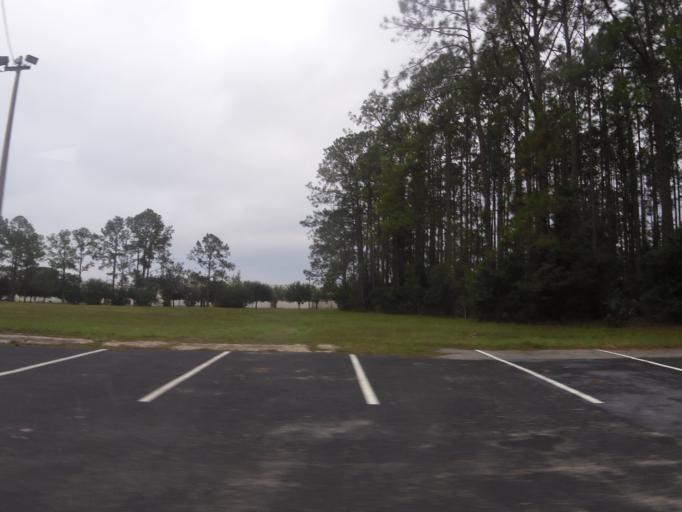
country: US
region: Florida
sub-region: Duval County
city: Baldwin
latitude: 30.2268
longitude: -81.8855
